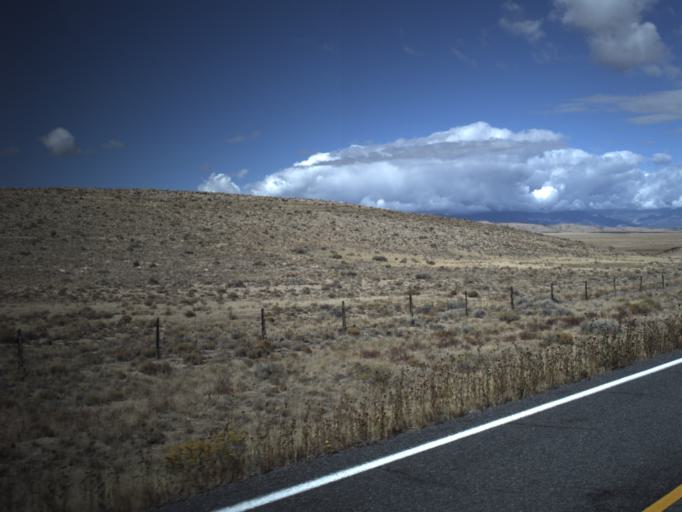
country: US
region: Utah
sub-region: Beaver County
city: Milford
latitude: 38.6238
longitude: -113.8490
